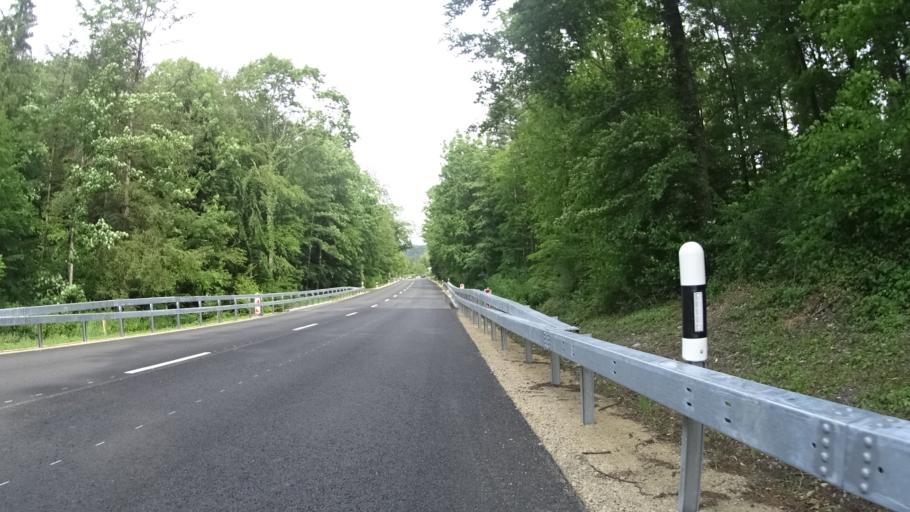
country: DE
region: Baden-Wuerttemberg
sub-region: Freiburg Region
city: Murg
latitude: 47.5494
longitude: 8.0279
